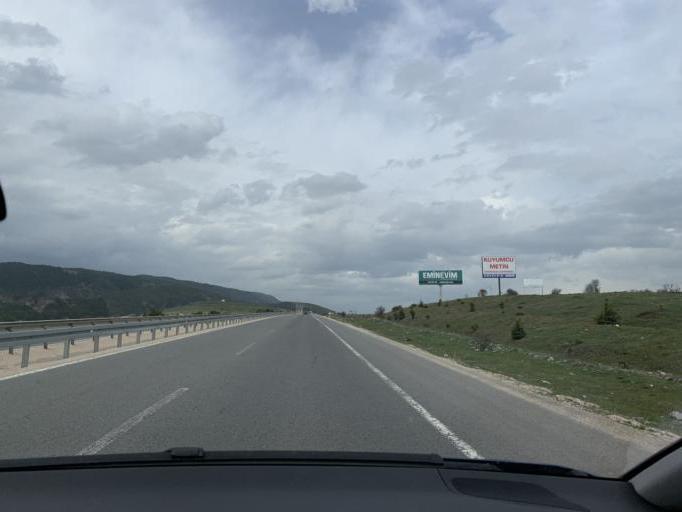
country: TR
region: Bolu
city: Gerede
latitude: 40.7943
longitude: 32.1482
